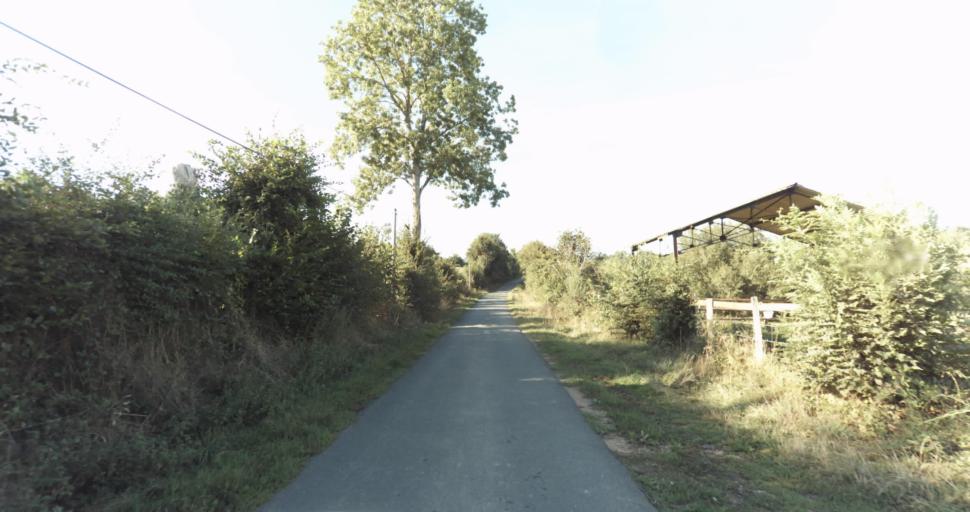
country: FR
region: Lower Normandy
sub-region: Departement de l'Orne
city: Vimoutiers
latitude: 48.8889
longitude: 0.1319
